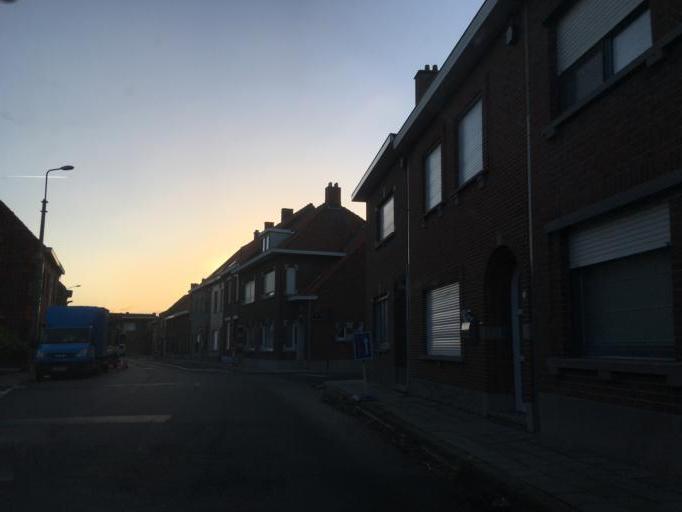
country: BE
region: Flanders
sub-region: Provincie West-Vlaanderen
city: Izegem
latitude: 50.9242
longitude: 3.2279
